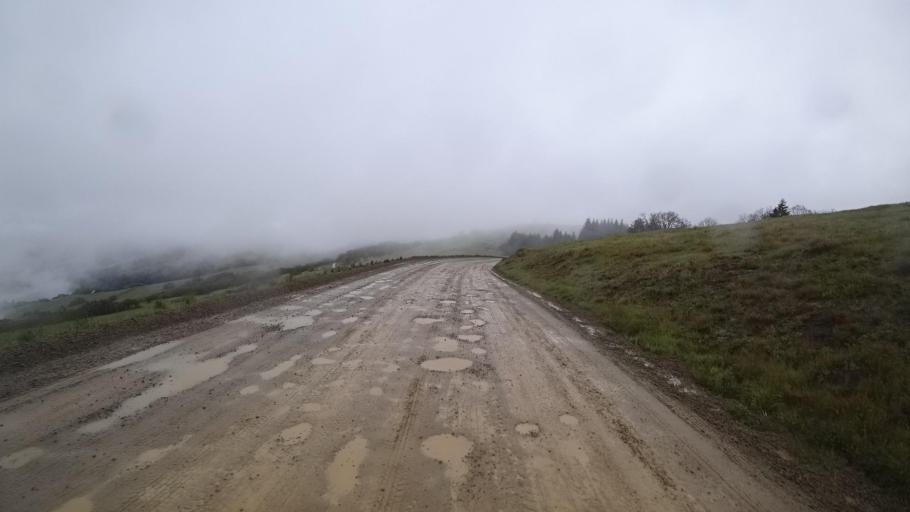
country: US
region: California
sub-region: Humboldt County
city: Westhaven-Moonstone
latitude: 41.1471
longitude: -123.8726
